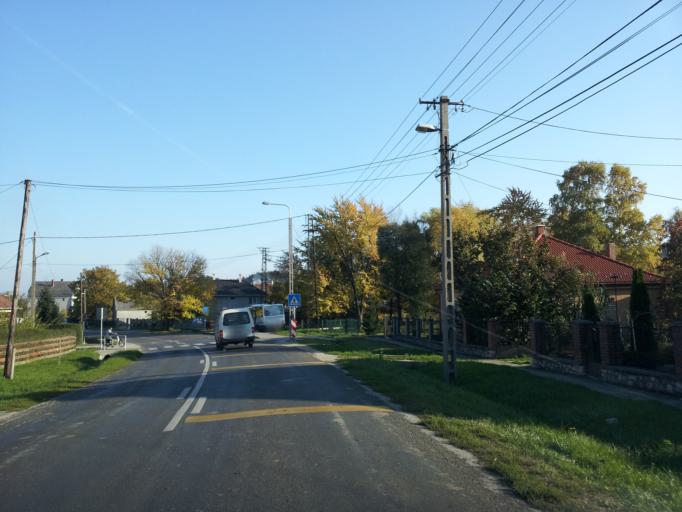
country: HU
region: Fejer
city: Bodajk
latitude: 47.3228
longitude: 18.2250
